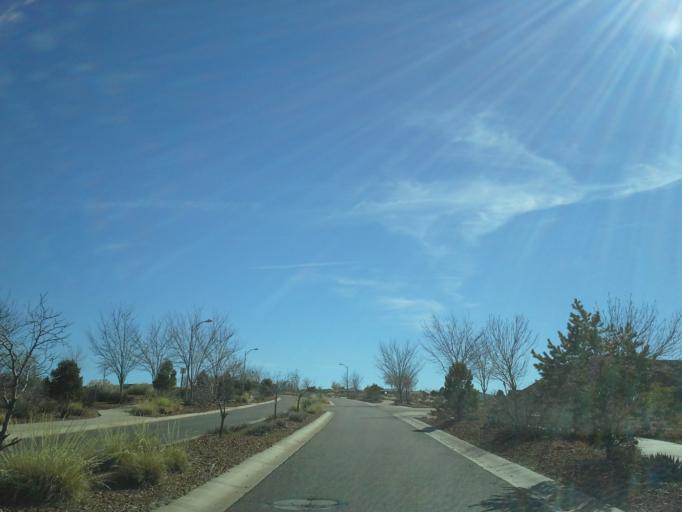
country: US
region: Arizona
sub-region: Coconino County
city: Page
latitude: 36.9351
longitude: -111.4640
